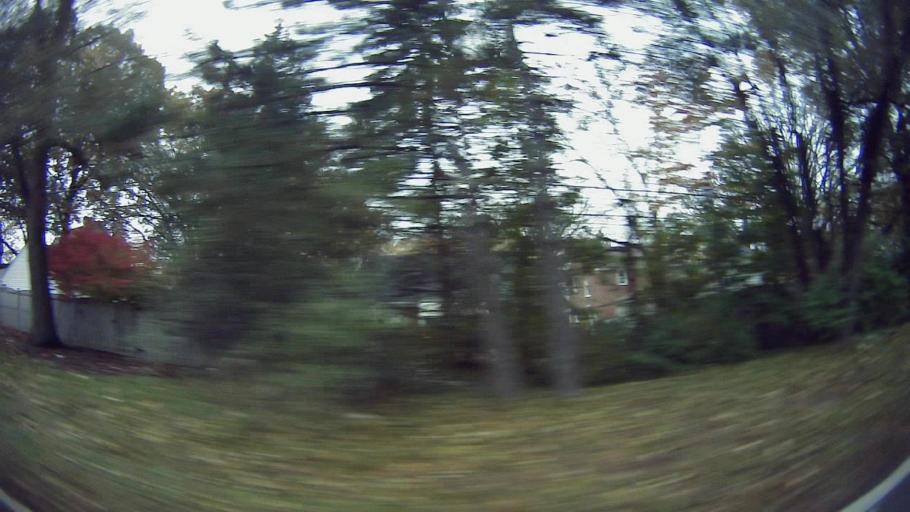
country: US
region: Michigan
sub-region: Wayne County
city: Dearborn Heights
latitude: 42.3076
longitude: -83.2720
